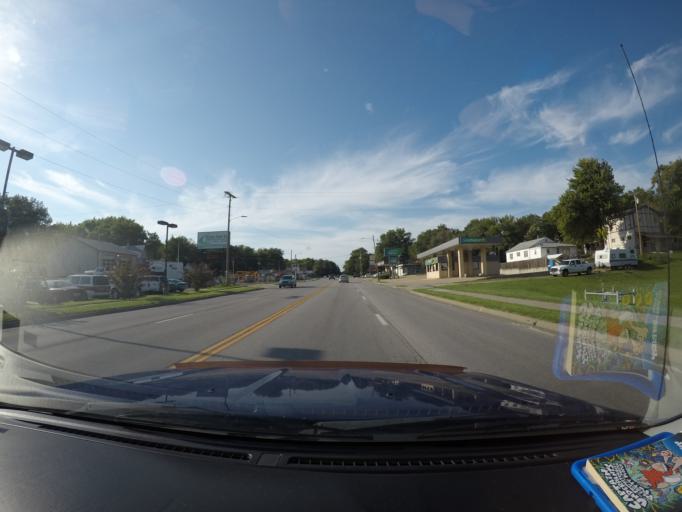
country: US
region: Kansas
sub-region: Leavenworth County
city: Leavenworth
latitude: 39.3048
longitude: -94.9097
